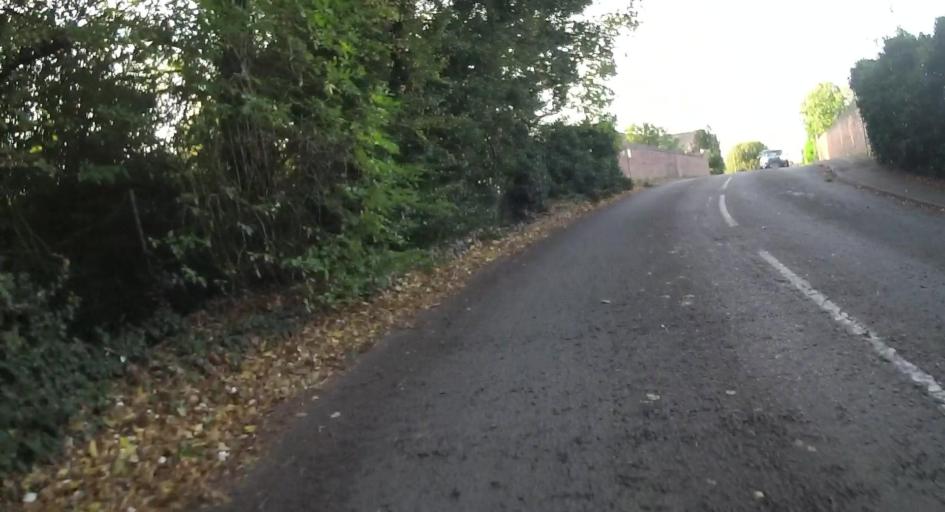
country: GB
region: England
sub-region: Surrey
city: Frimley
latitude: 51.3001
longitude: -0.7250
